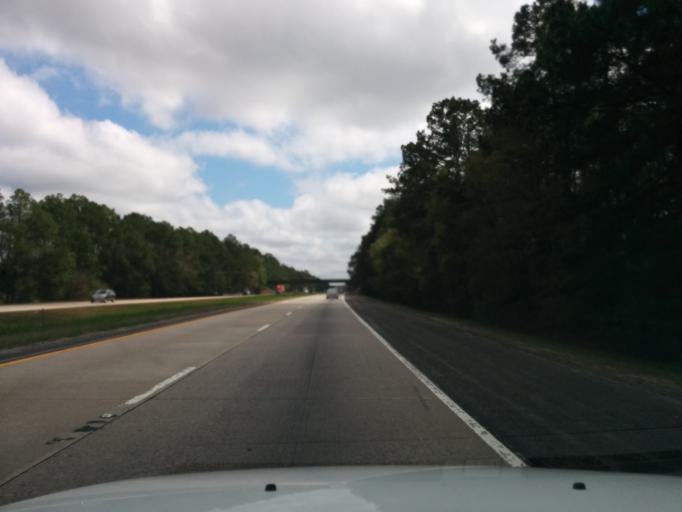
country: US
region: Georgia
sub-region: Chatham County
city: Bloomingdale
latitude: 32.1619
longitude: -81.4353
